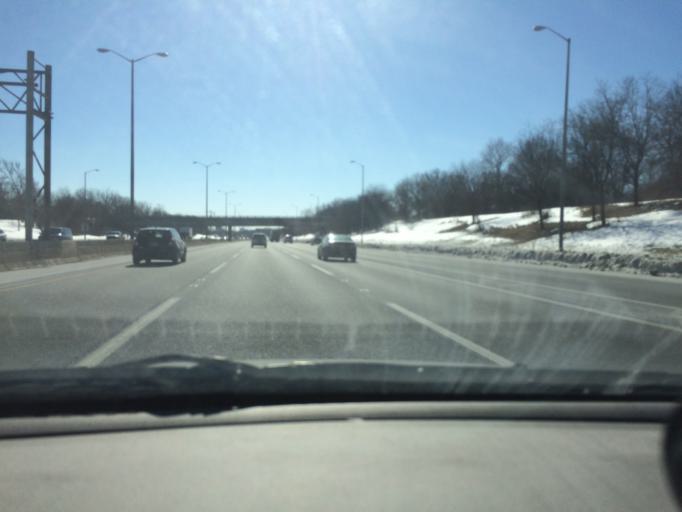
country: US
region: Illinois
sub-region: DuPage County
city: Glendale Heights
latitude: 41.8995
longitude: -88.0380
